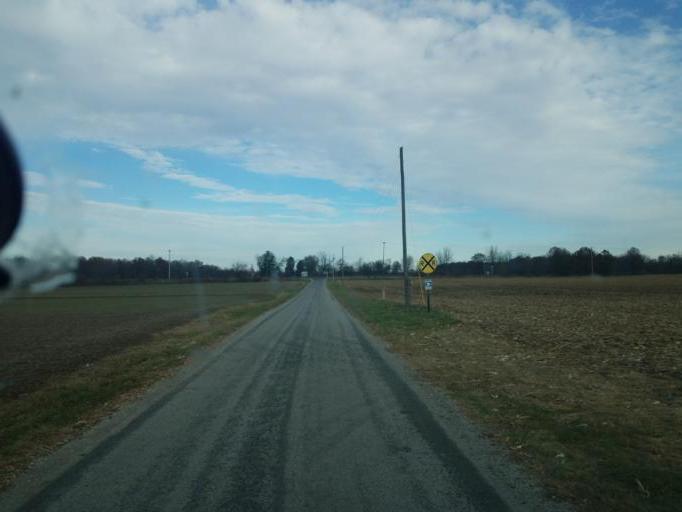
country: US
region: Ohio
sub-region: Morrow County
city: Mount Gilead
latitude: 40.6509
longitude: -82.9387
